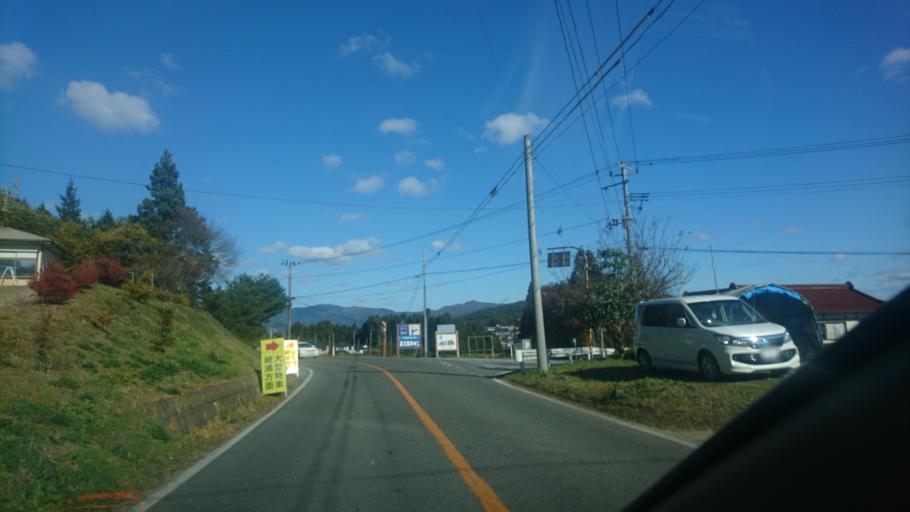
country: JP
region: Iwate
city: Ofunato
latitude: 38.9938
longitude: 141.7074
